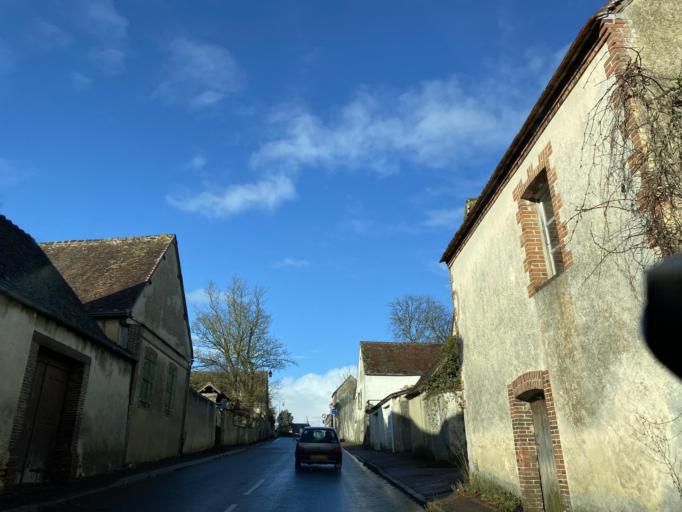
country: FR
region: Centre
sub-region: Departement d'Eure-et-Loir
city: Brezolles
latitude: 48.6322
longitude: 1.1476
